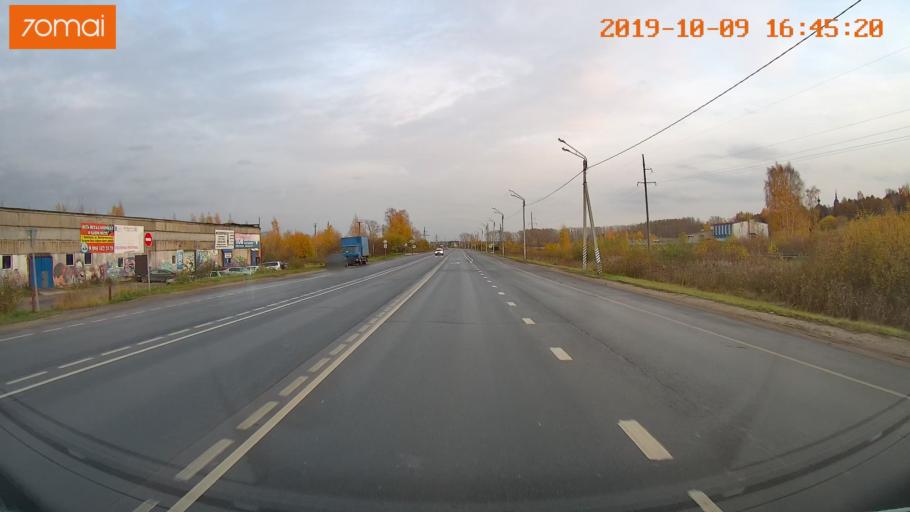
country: RU
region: Kostroma
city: Volgorechensk
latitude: 57.4469
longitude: 41.1533
